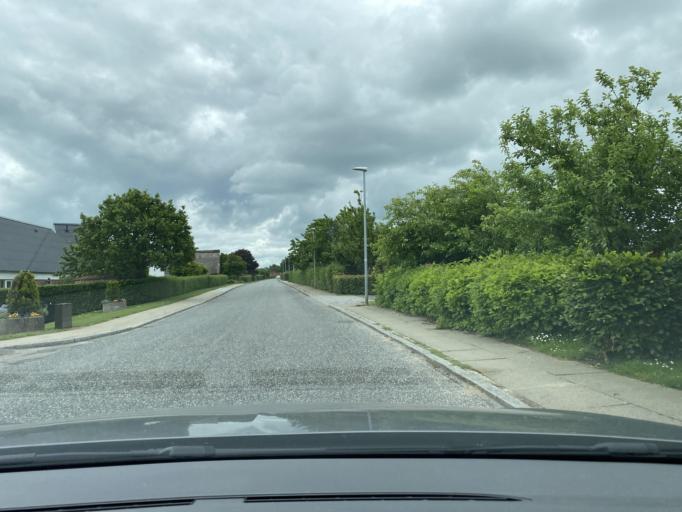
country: DK
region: South Denmark
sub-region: Vejle Kommune
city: Vejle
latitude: 55.6585
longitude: 9.4948
